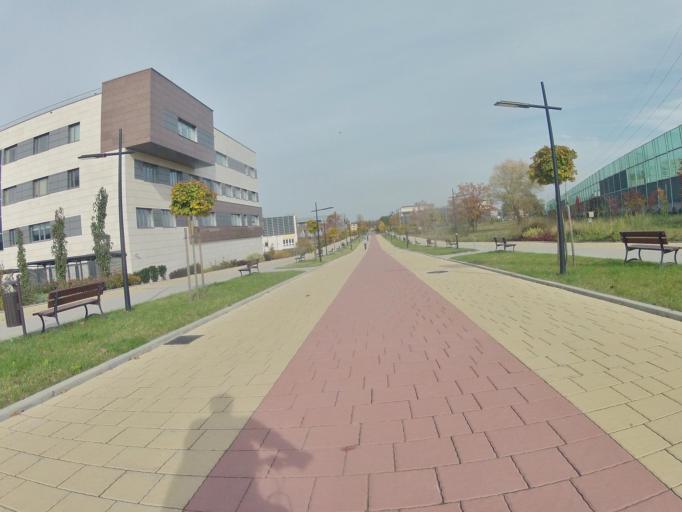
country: PL
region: Lesser Poland Voivodeship
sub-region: Krakow
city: Sidzina
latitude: 50.0262
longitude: 19.9031
